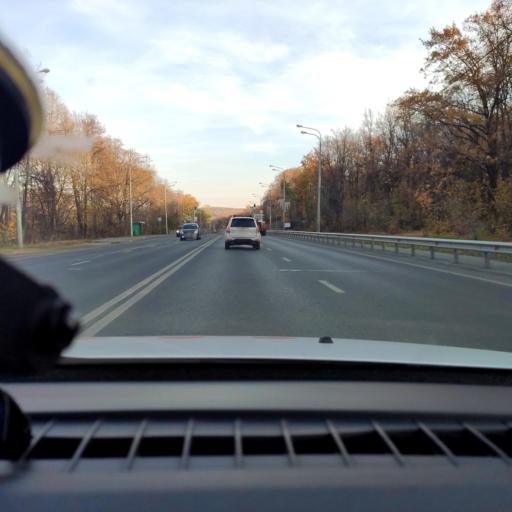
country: RU
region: Samara
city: Samara
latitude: 53.2944
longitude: 50.2248
